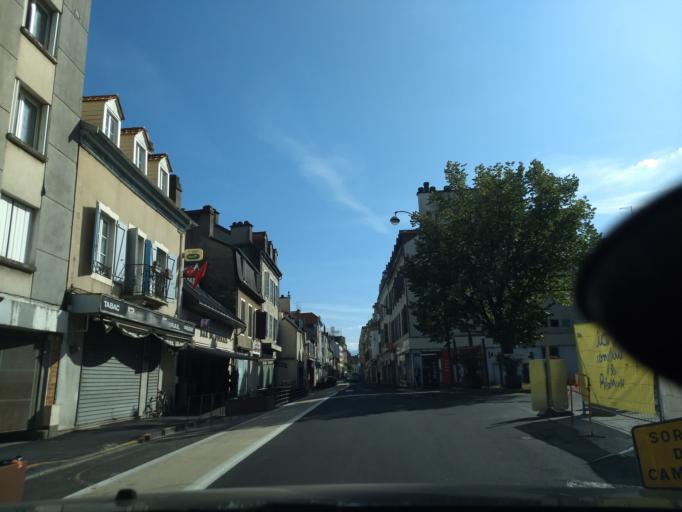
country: FR
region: Aquitaine
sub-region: Departement des Pyrenees-Atlantiques
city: Pau
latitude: 43.3029
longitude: -0.3688
